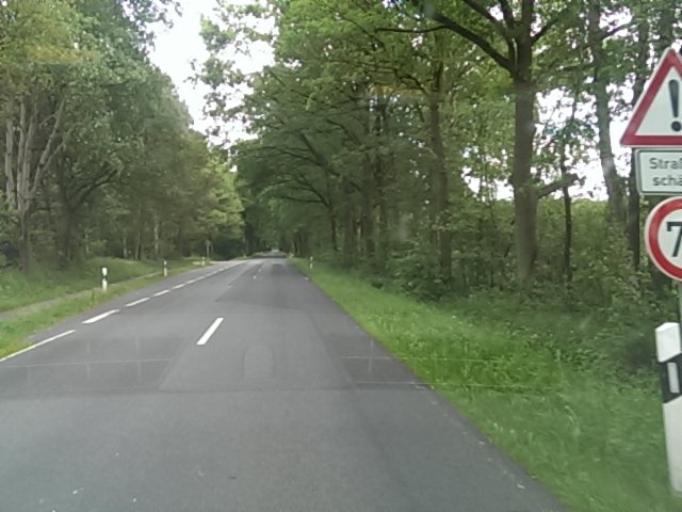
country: DE
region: Lower Saxony
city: Hermannsburg
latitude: 52.7947
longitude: 10.0968
